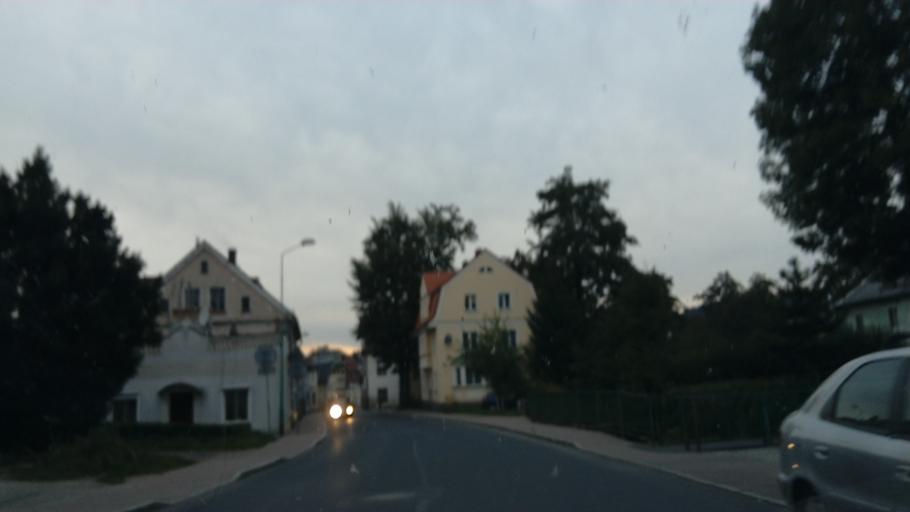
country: PL
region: Lower Silesian Voivodeship
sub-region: Powiat jeleniogorski
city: Kowary
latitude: 50.7967
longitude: 15.8309
